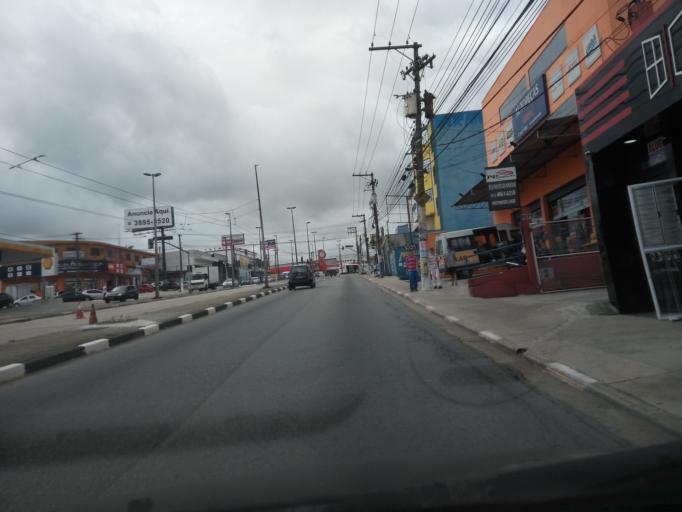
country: BR
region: Sao Paulo
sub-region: Sao Bernardo Do Campo
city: Sao Bernardo do Campo
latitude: -23.6914
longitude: -46.5883
